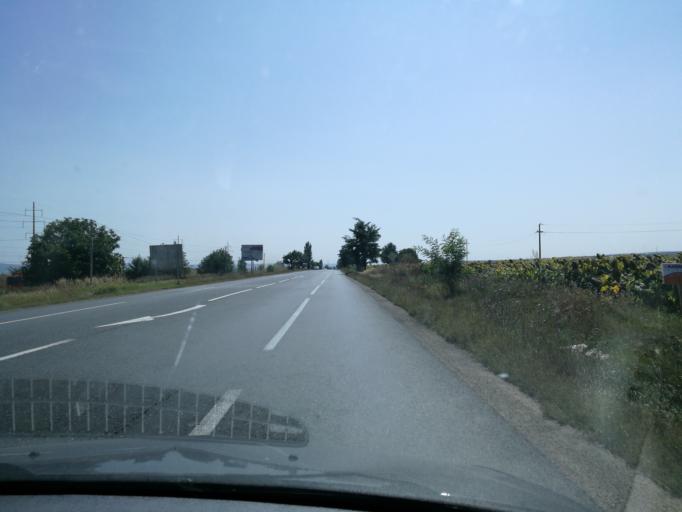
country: RO
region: Bacau
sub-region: Comuna Sascut
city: Sascut
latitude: 46.2028
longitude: 27.1115
